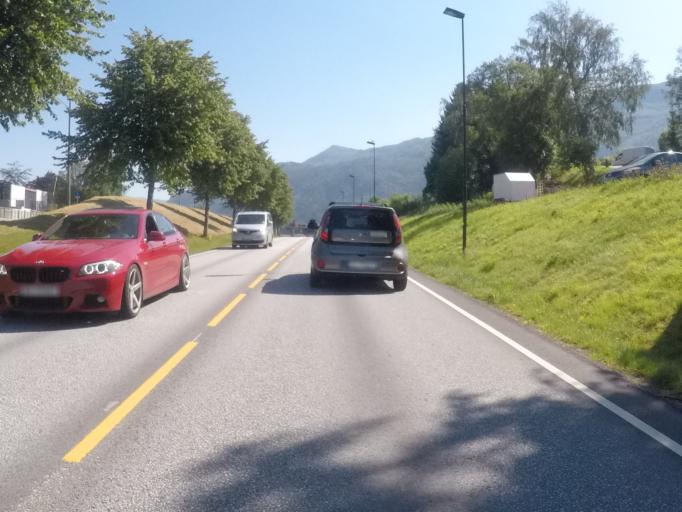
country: NO
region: Sogn og Fjordane
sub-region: Eid
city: Nordfjordeid
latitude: 61.9111
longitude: 5.9921
